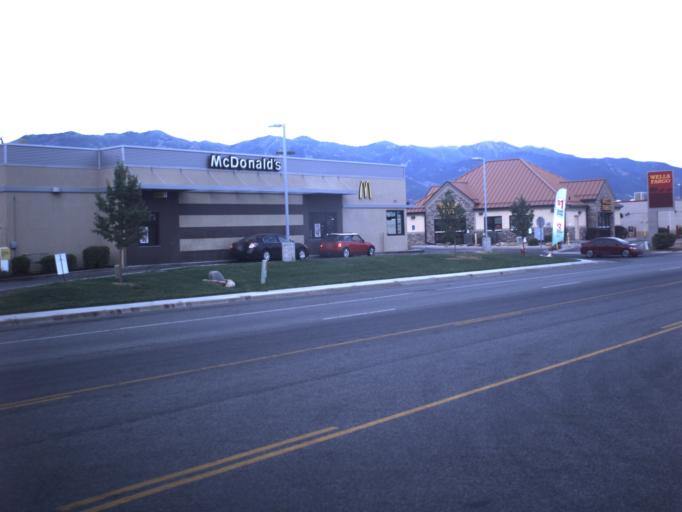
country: US
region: Utah
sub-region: Davis County
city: Clearfield
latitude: 41.0911
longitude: -112.0032
